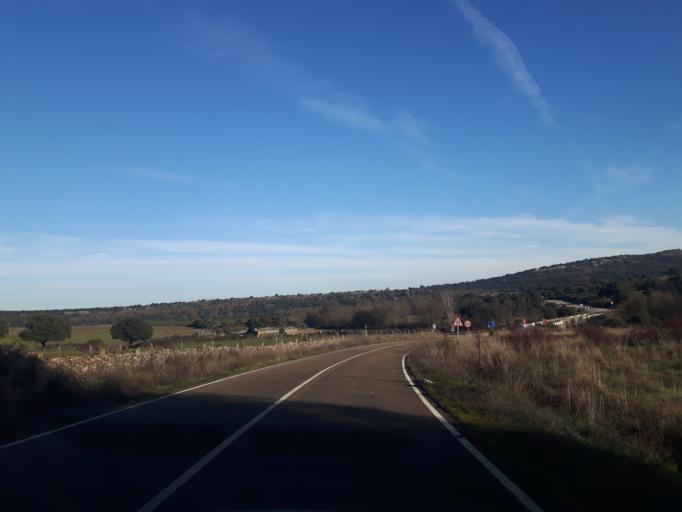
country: ES
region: Castille and Leon
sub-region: Provincia de Salamanca
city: Olmedo de Camaces
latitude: 40.8834
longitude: -6.6260
